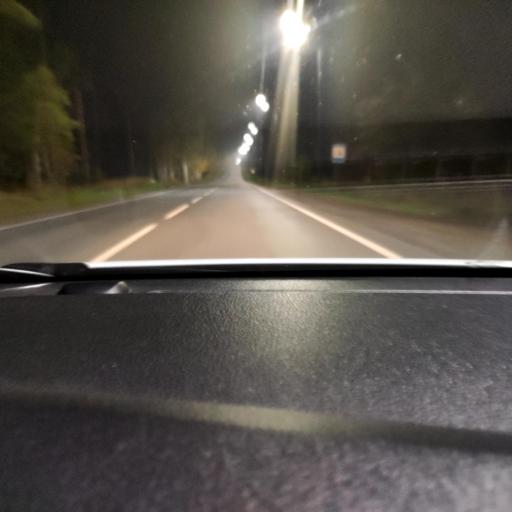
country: RU
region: Tatarstan
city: Stolbishchi
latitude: 55.6347
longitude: 49.0827
